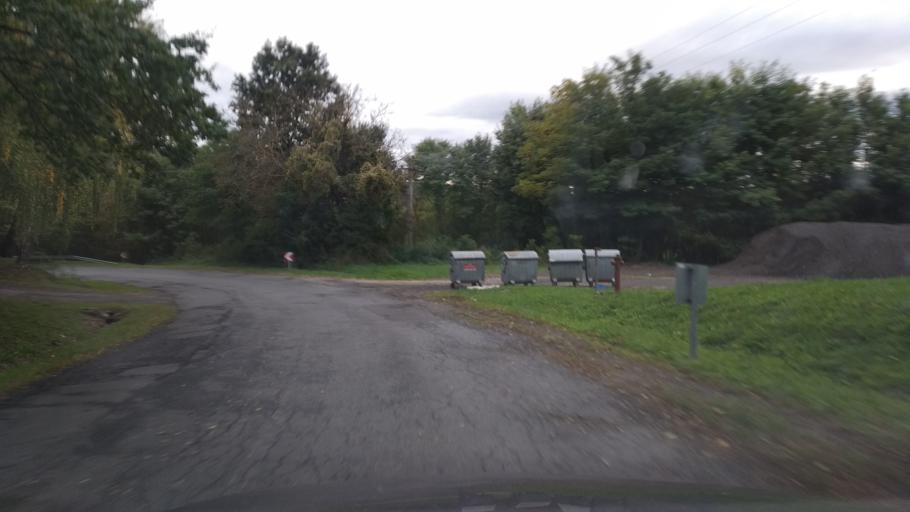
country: HU
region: Zala
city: Becsehely
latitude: 46.5287
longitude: 16.7344
